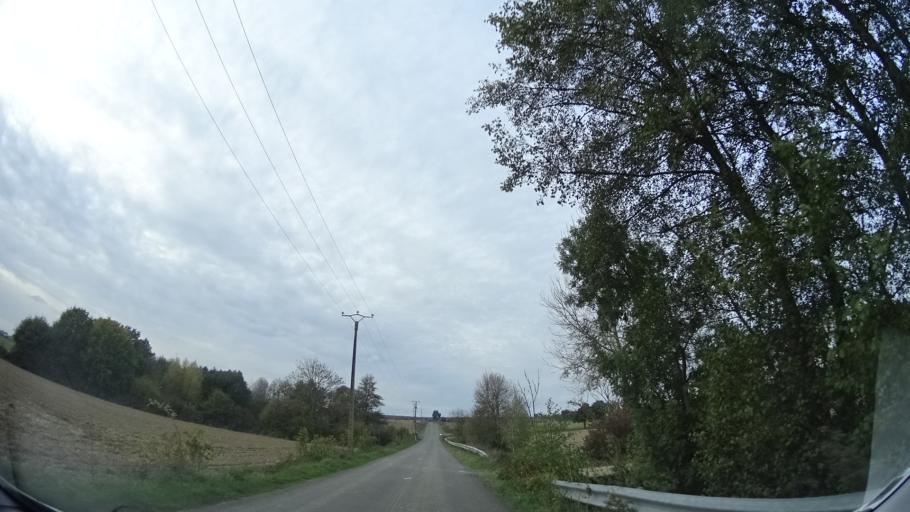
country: FR
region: Brittany
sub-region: Departement d'Ille-et-Vilaine
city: Boisgervilly
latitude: 48.1032
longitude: -2.1200
